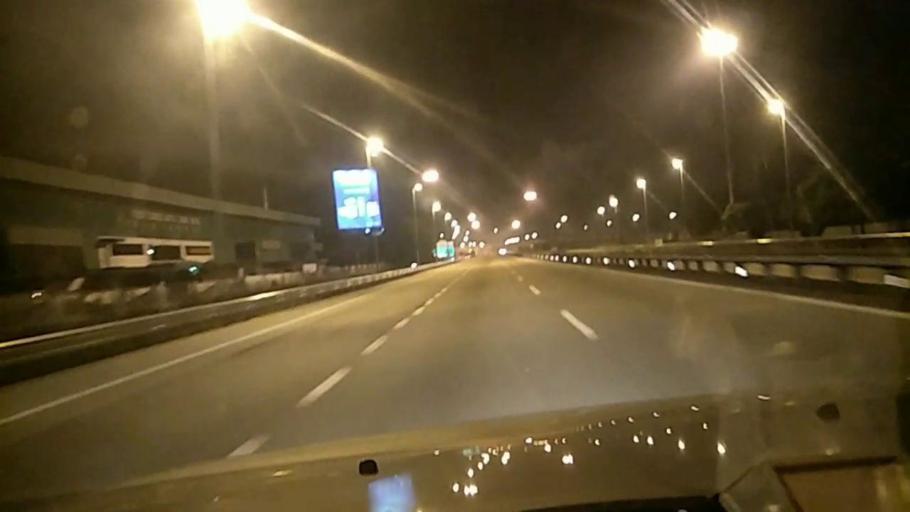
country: MY
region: Penang
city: Juru
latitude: 5.2463
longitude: 100.4733
